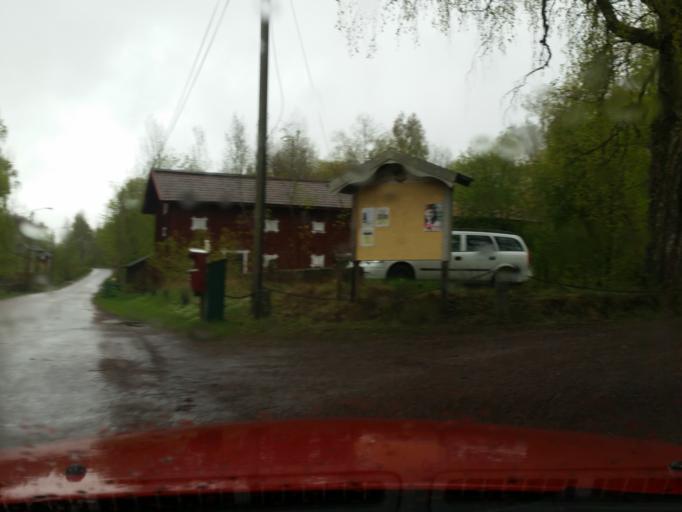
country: SE
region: Dalarna
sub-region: Saters Kommun
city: Saeter
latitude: 60.3604
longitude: 15.7901
